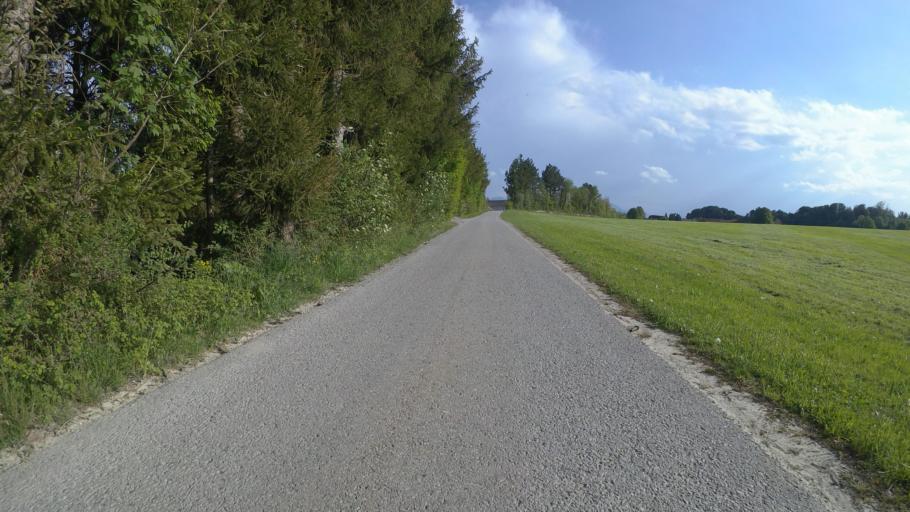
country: DE
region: Bavaria
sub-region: Upper Bavaria
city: Chieming
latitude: 47.8962
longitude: 12.5677
